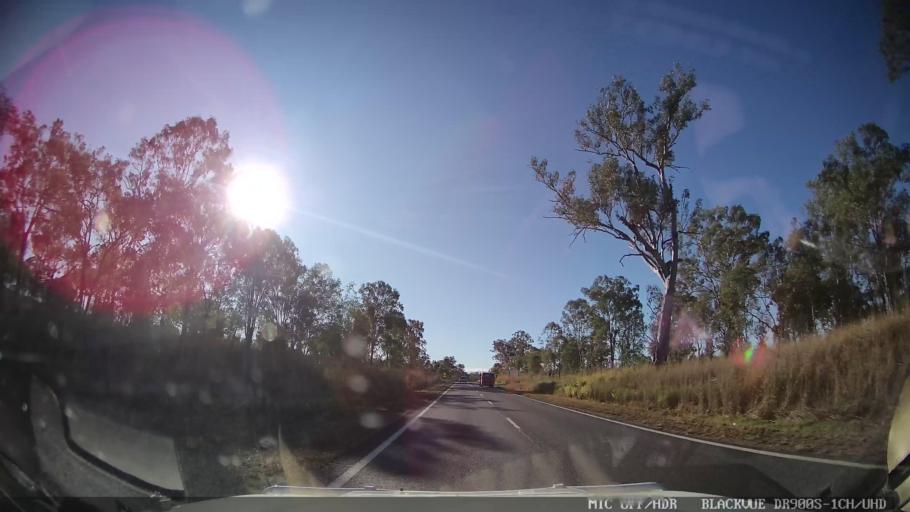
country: AU
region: Queensland
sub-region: Bundaberg
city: Sharon
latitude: -24.8267
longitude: 151.7073
